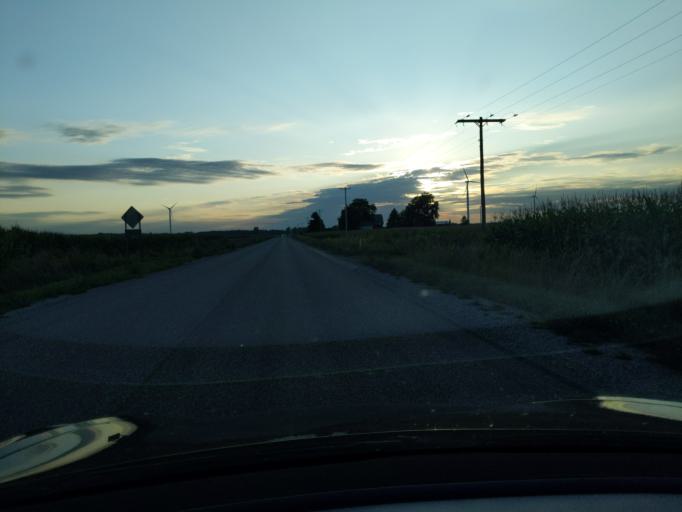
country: US
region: Michigan
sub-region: Gratiot County
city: Saint Louis
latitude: 43.3790
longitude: -84.5505
